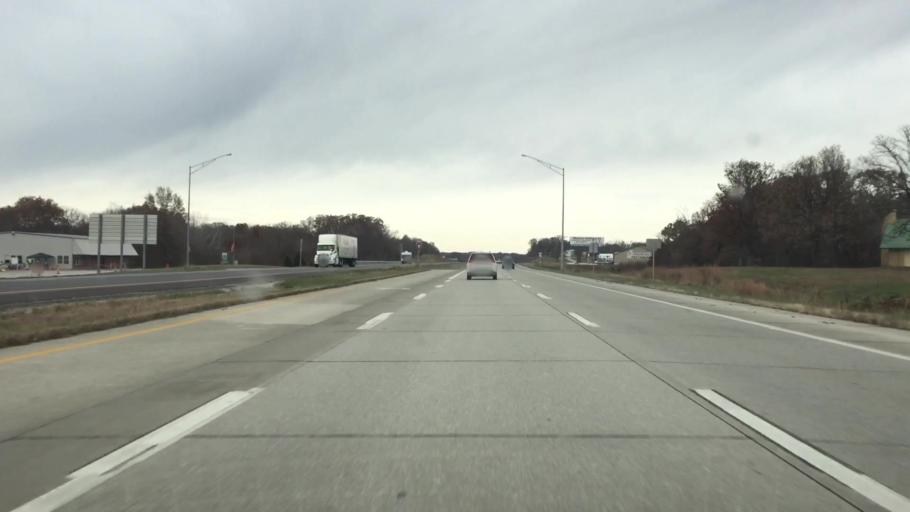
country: US
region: Missouri
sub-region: Saint Clair County
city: Osceola
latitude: 38.0749
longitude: -93.7011
